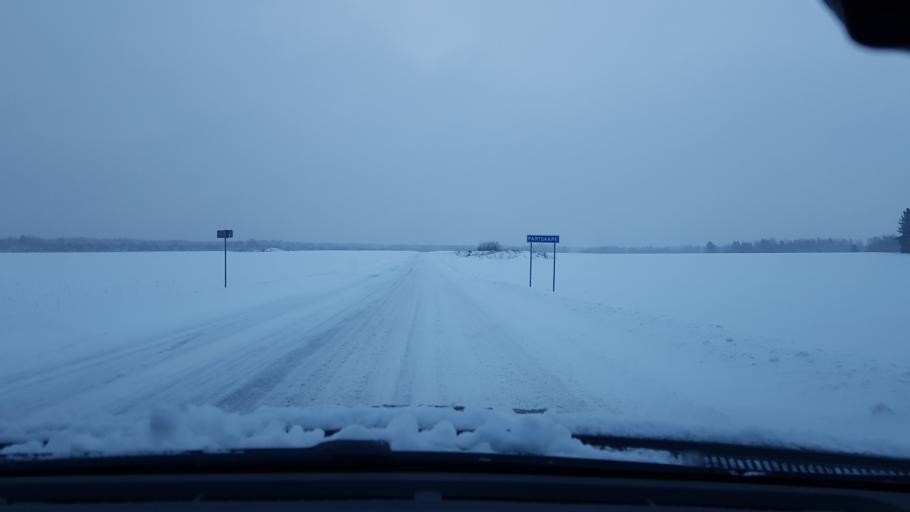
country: EE
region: Harju
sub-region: Anija vald
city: Kehra
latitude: 59.3841
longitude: 25.3104
